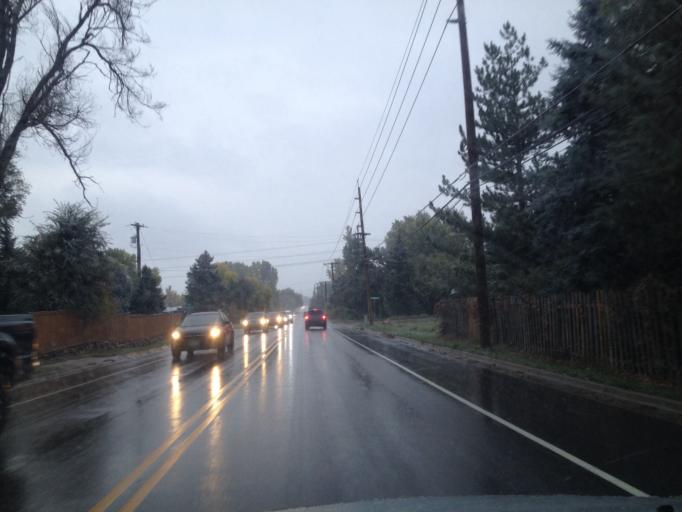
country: US
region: Colorado
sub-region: Boulder County
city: Superior
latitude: 39.9889
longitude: -105.1753
